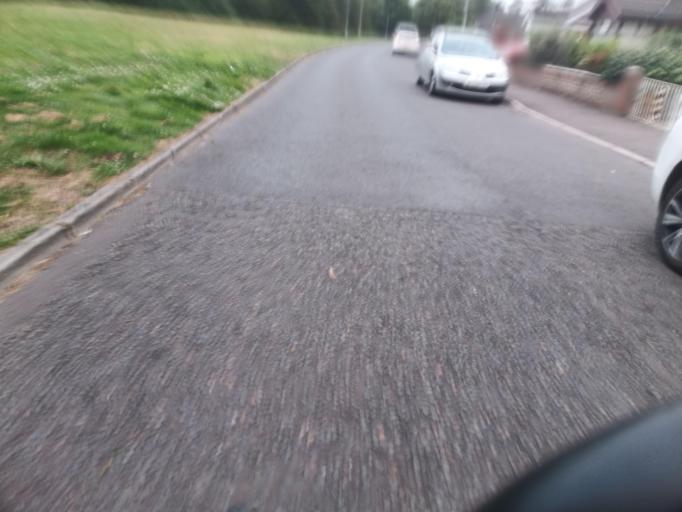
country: GB
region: Northern Ireland
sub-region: Ards District
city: Comber
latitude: 54.5525
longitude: -5.7300
